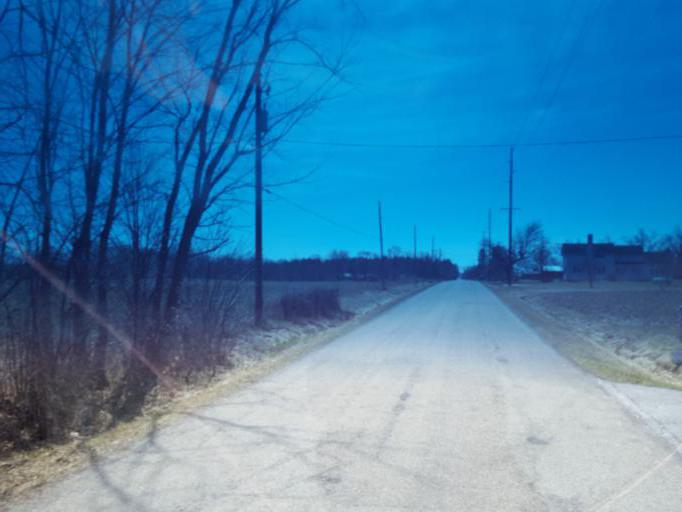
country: US
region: Ohio
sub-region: Crawford County
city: Galion
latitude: 40.7282
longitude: -82.7460
